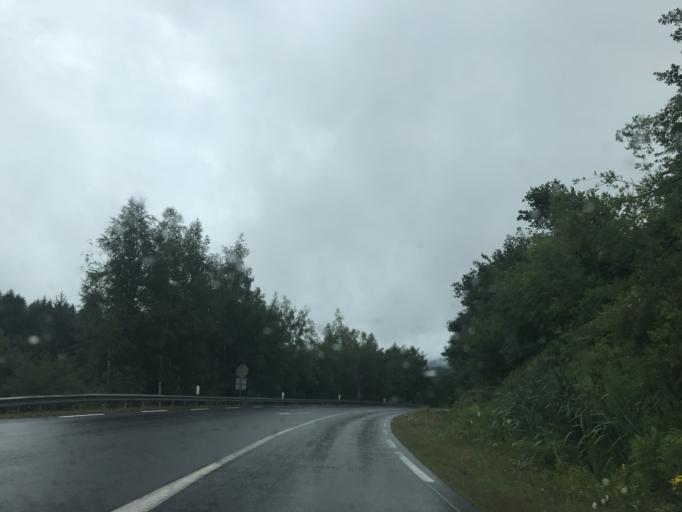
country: FR
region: Auvergne
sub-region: Departement du Puy-de-Dome
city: Job
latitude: 45.6302
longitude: 3.7122
